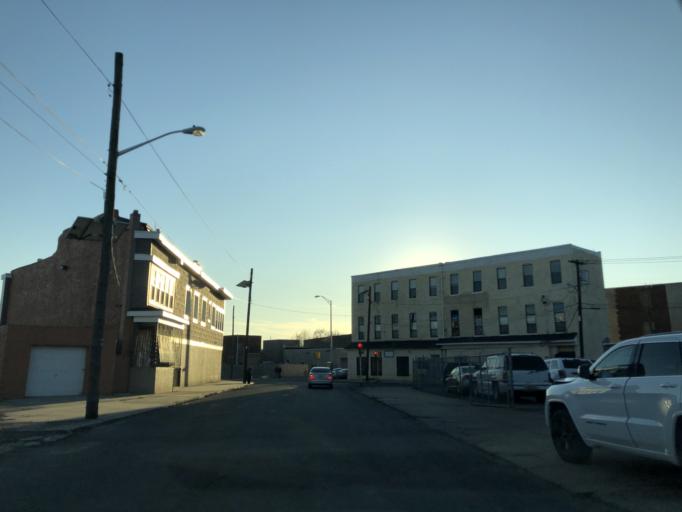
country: US
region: New Jersey
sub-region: Camden County
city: Camden
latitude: 39.9313
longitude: -75.1216
